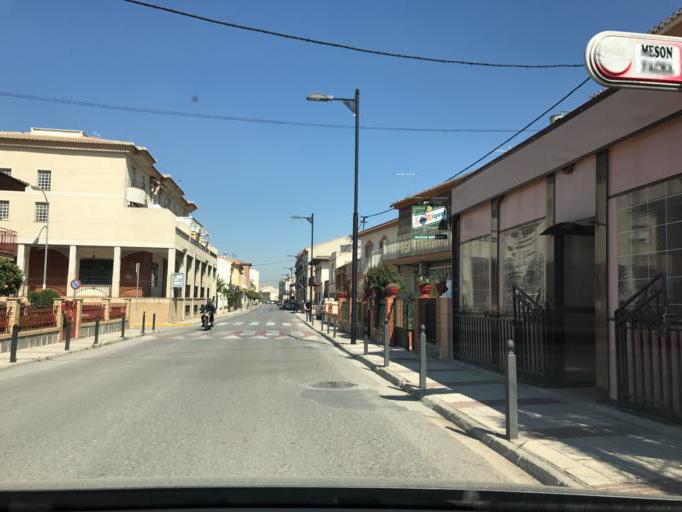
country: ES
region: Andalusia
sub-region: Provincia de Granada
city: Chauchina
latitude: 37.1954
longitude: -3.7738
